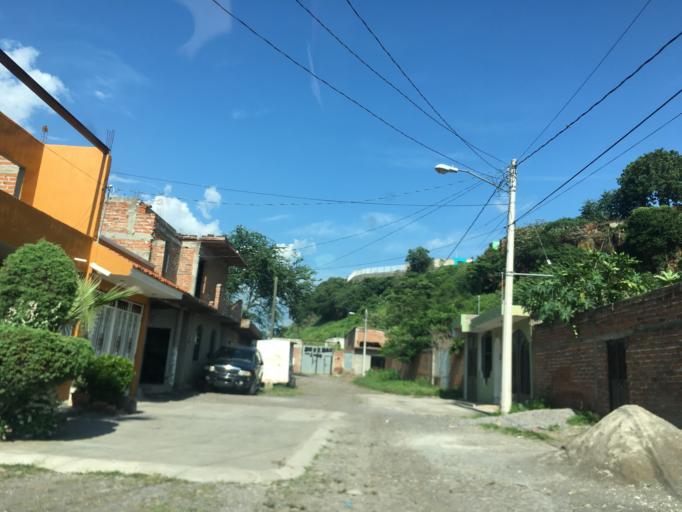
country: MX
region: Nayarit
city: Ixtlan del Rio
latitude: 21.0431
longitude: -104.3613
